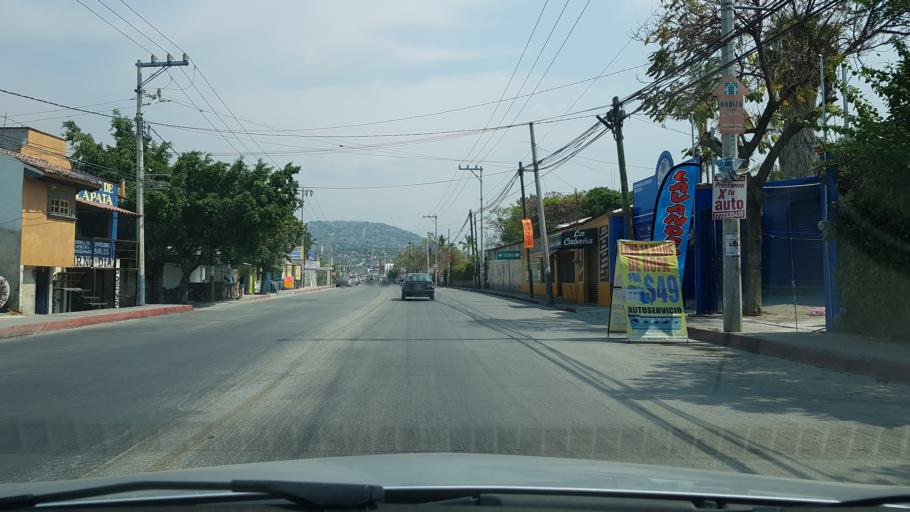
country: MX
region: Morelos
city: Emiliano Zapata
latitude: 18.8277
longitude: -99.1880
